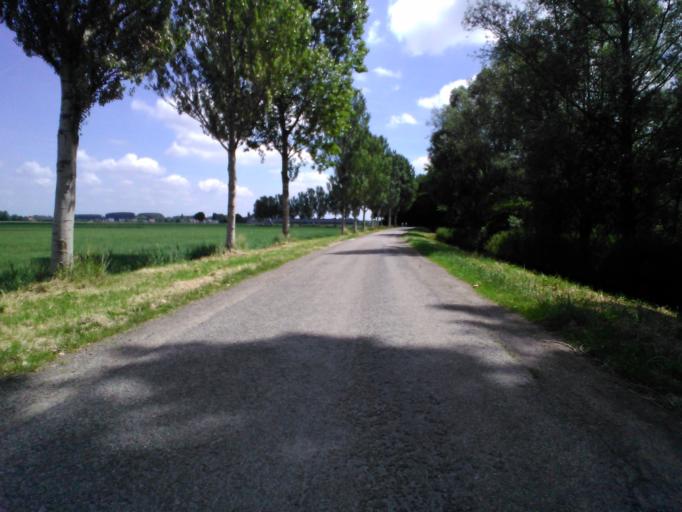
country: NL
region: North Brabant
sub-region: Gemeente Woudrichem
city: Almkerk
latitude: 51.7842
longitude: 4.9893
